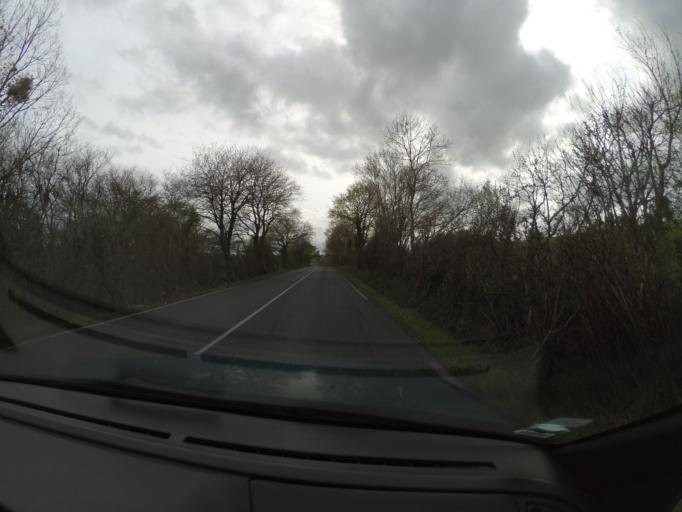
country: FR
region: Pays de la Loire
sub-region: Departement de Maine-et-Loire
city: Saint-Laurent-des-Autels
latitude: 47.3066
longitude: -1.1624
